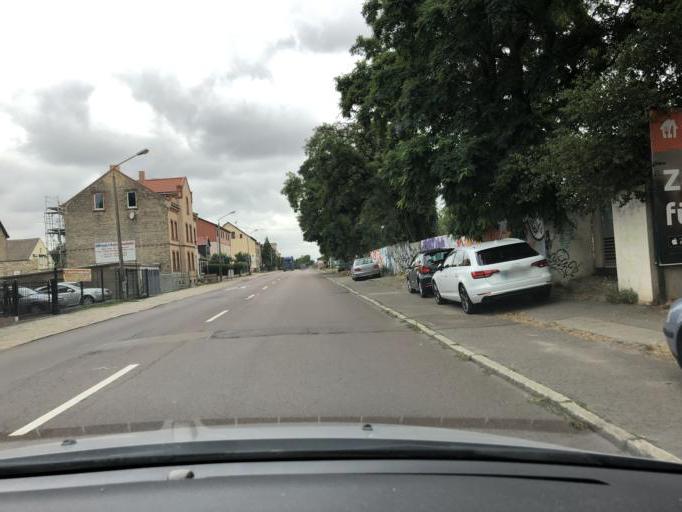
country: DE
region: Saxony-Anhalt
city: Dollnitz
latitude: 51.4201
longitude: 12.0086
